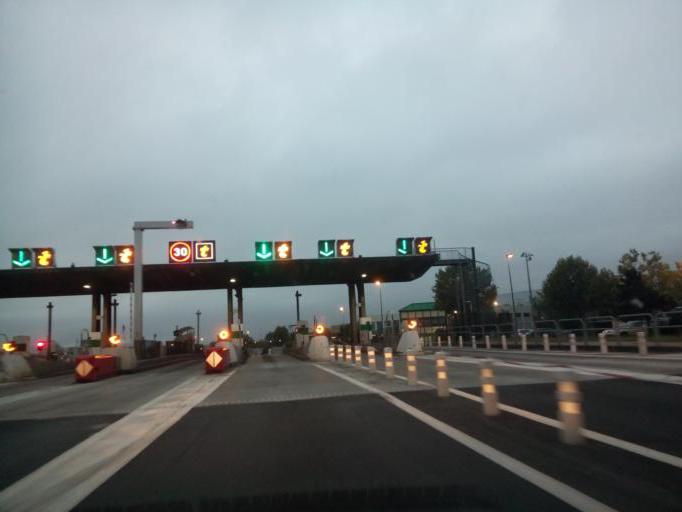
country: FR
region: Rhone-Alpes
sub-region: Departement de l'Isere
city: Saint-Quentin-Fallavier
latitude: 45.6479
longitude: 5.1196
